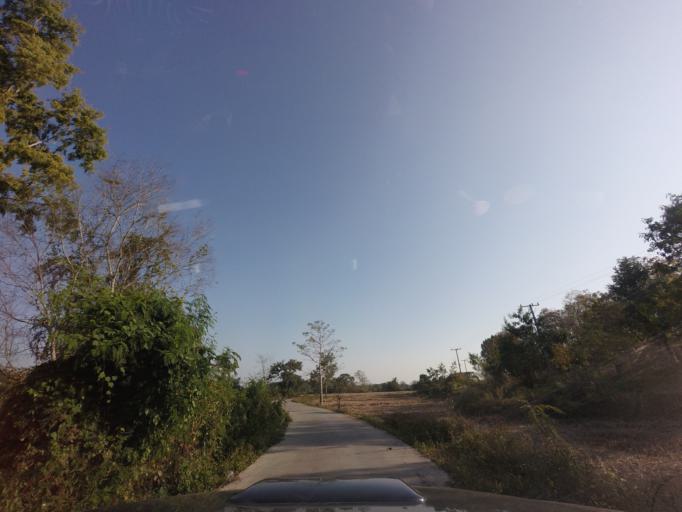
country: TH
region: Chiang Mai
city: San Sai
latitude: 18.9045
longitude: 99.1182
